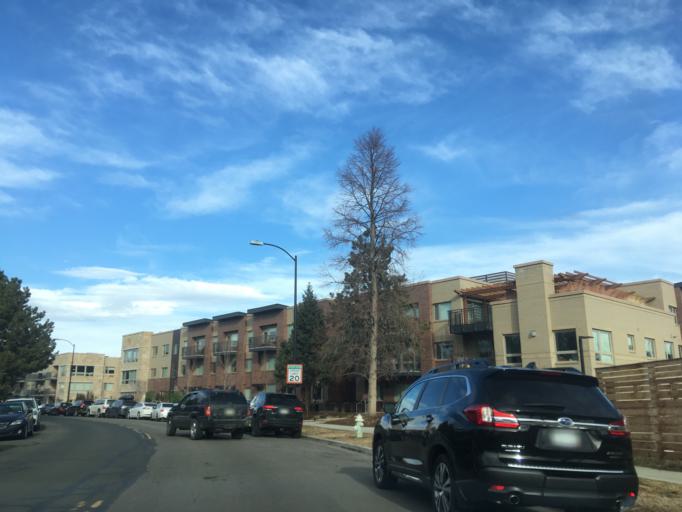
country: US
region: Colorado
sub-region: Boulder County
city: Boulder
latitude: 40.0129
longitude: -105.2322
